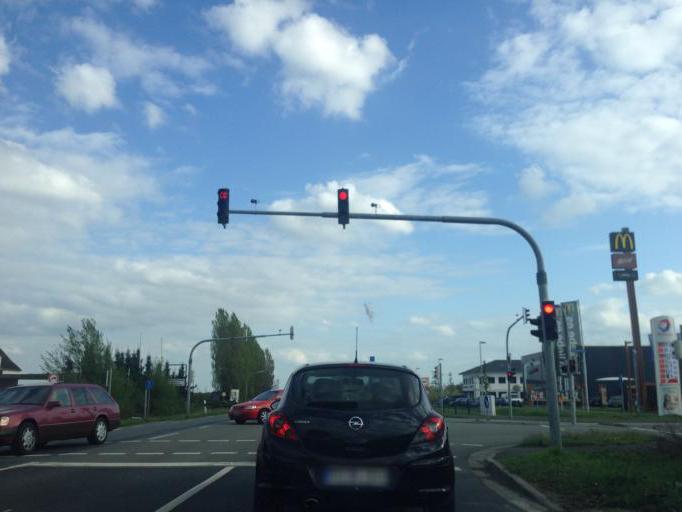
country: DE
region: Lower Saxony
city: Klein Schwulper
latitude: 52.3387
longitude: 10.4185
